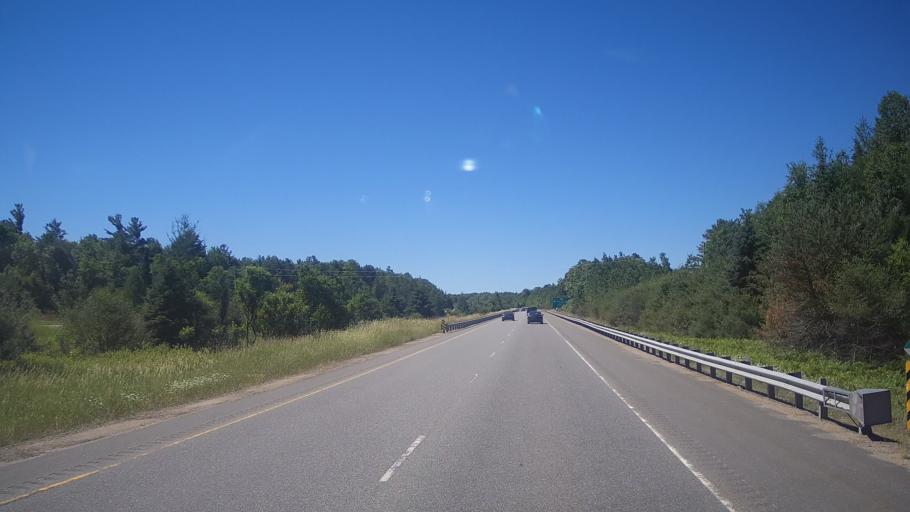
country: CA
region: Ontario
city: Huntsville
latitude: 45.2293
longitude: -79.3078
